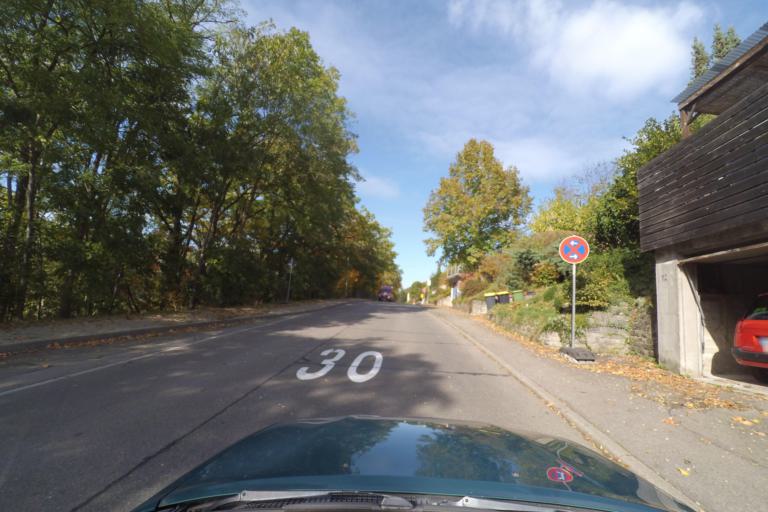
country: DE
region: Baden-Wuerttemberg
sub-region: Karlsruhe Region
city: Nagold
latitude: 48.5581
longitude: 8.7287
